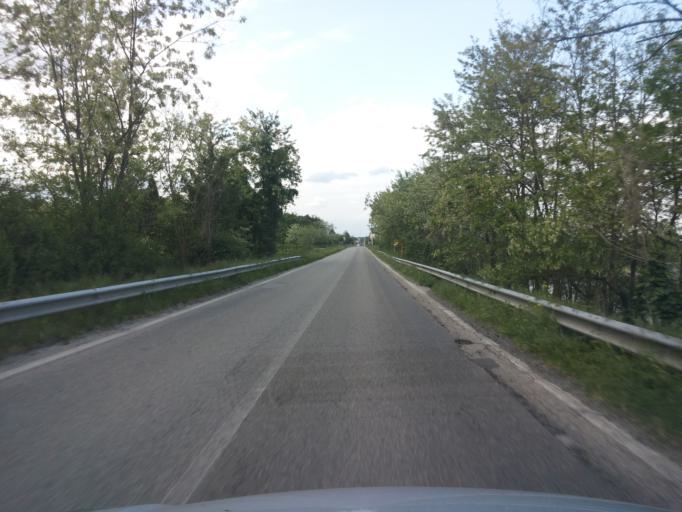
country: IT
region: Piedmont
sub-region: Provincia di Biella
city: Cavaglia
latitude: 45.3860
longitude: 8.0855
